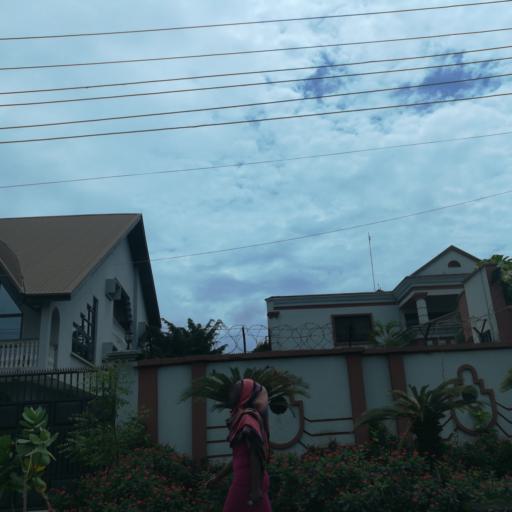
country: NG
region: Lagos
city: Ikoyi
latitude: 6.4446
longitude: 3.4597
